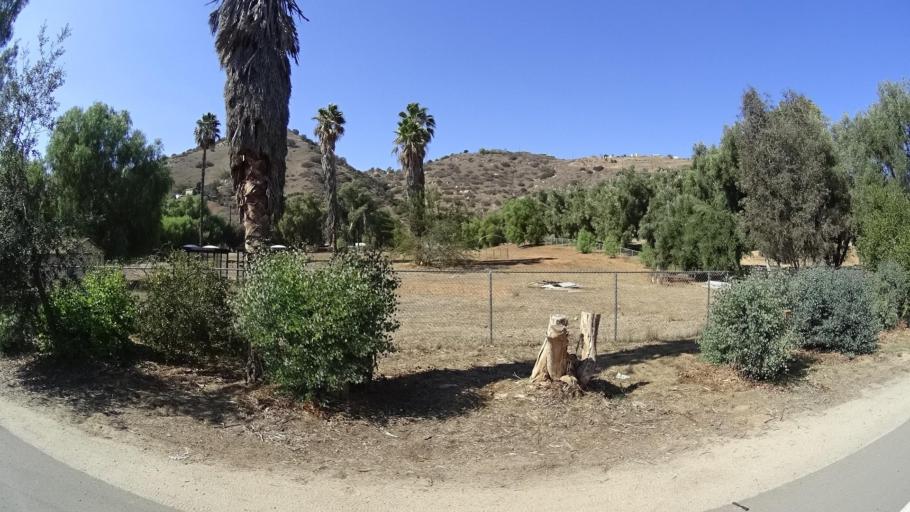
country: US
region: California
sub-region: San Diego County
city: Crest
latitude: 32.7979
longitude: -116.8460
